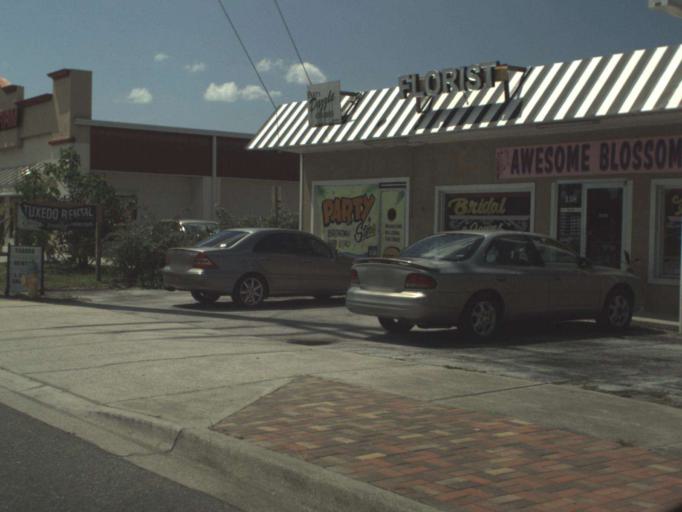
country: US
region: Florida
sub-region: Brevard County
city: Rockledge
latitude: 28.3572
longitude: -80.6967
